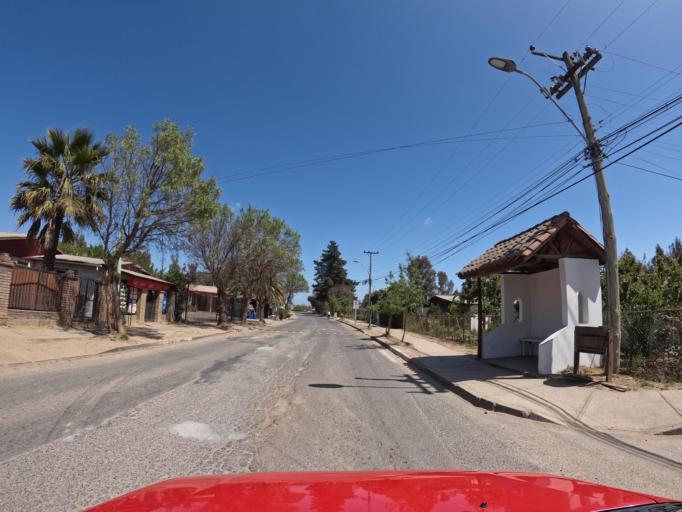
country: CL
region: O'Higgins
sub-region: Provincia de Colchagua
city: Santa Cruz
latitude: -34.7280
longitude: -71.6636
